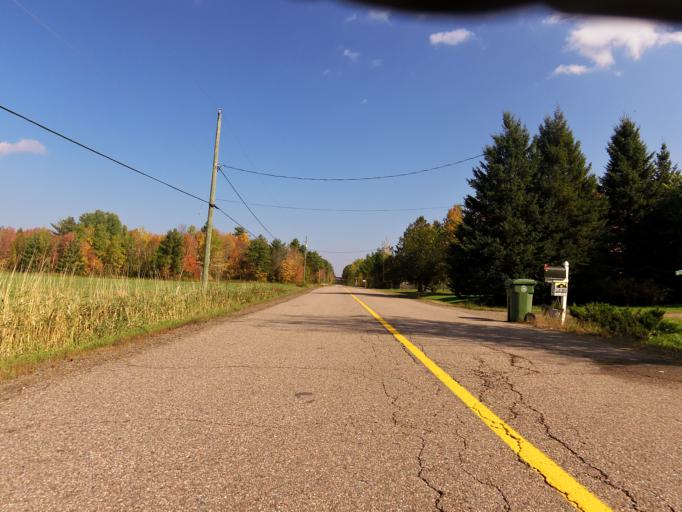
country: CA
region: Ontario
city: Petawawa
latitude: 45.8125
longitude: -77.2618
